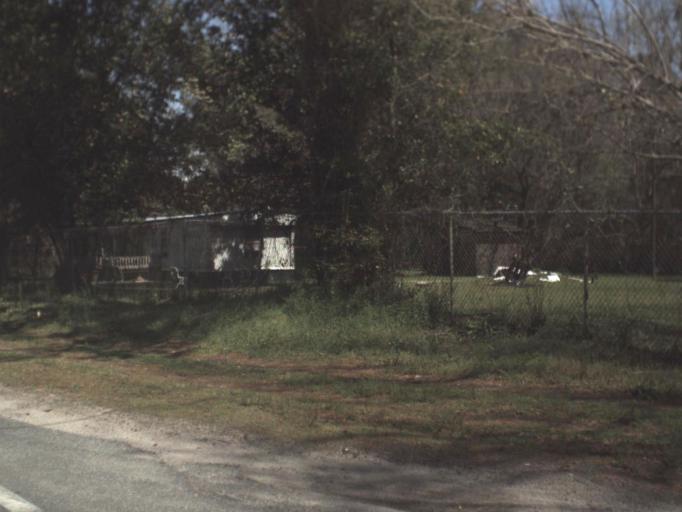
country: US
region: Florida
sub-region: Wakulla County
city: Crawfordville
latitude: 30.1393
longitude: -84.3879
